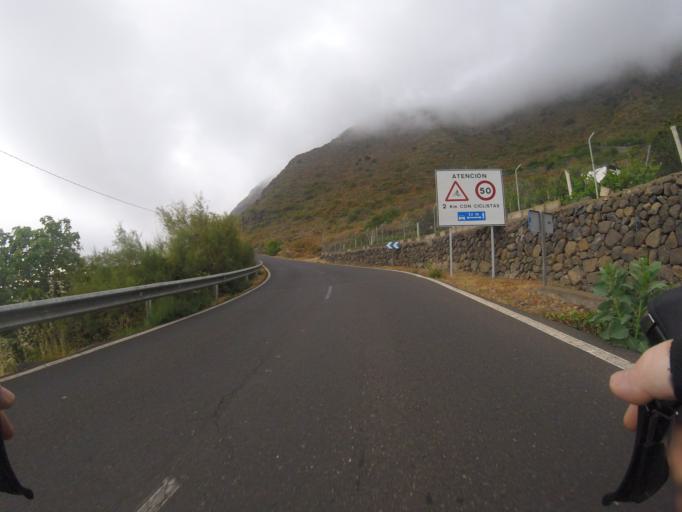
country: ES
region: Canary Islands
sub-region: Provincia de Santa Cruz de Tenerife
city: Guimar
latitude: 28.2969
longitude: -16.4172
